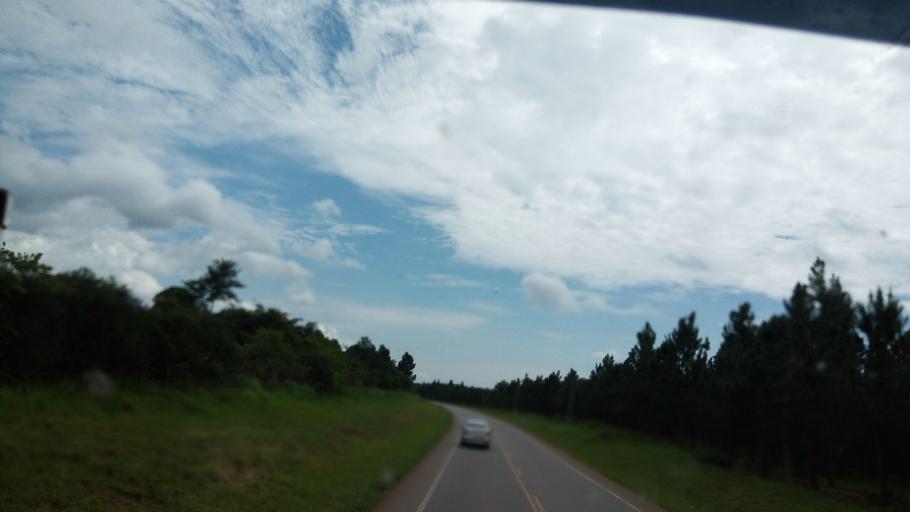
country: UG
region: Central Region
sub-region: Nakasongola District
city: Nakasongola
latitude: 1.2211
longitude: 32.4649
